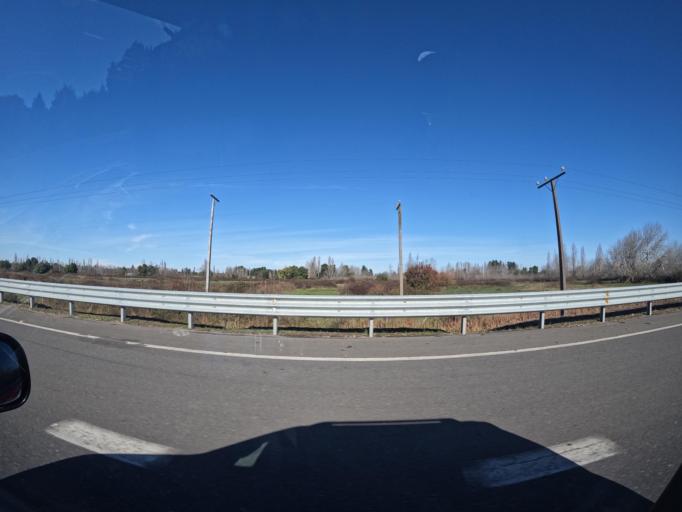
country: CL
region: Biobio
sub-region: Provincia de Biobio
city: Cabrero
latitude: -37.0279
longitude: -72.4435
